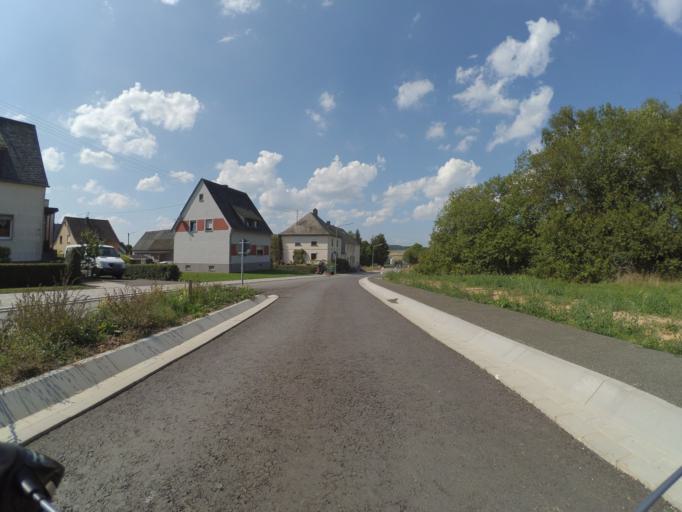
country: DE
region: Rheinland-Pfalz
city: Hochscheid
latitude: 49.8448
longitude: 7.1877
